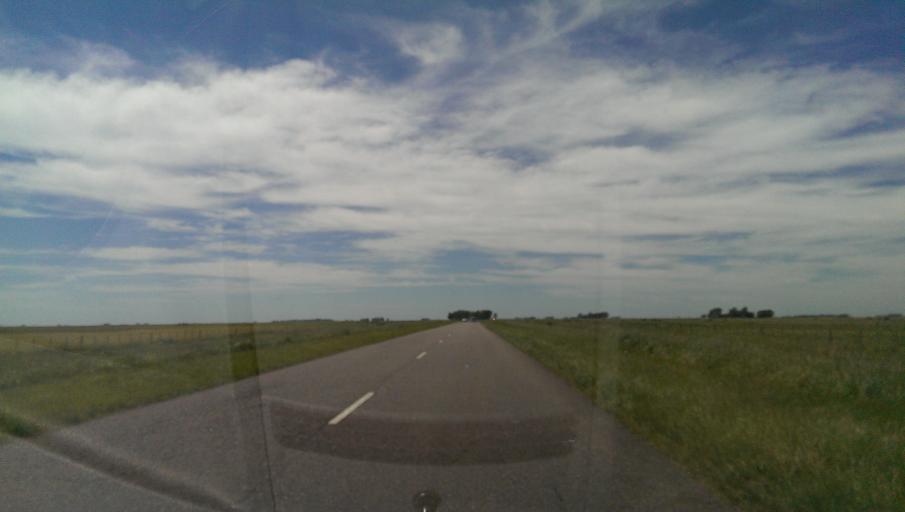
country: AR
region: Buenos Aires
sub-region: Partido de General La Madrid
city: General La Madrid
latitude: -37.4756
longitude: -61.1661
